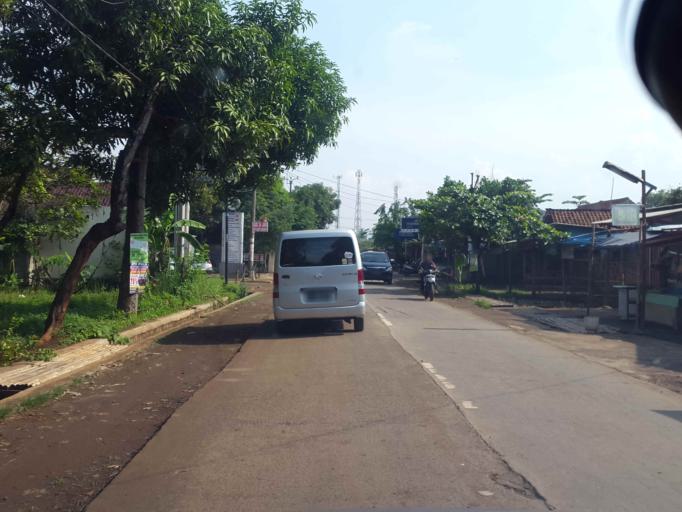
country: ID
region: West Java
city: Cileungsir
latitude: -6.3409
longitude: 107.0387
